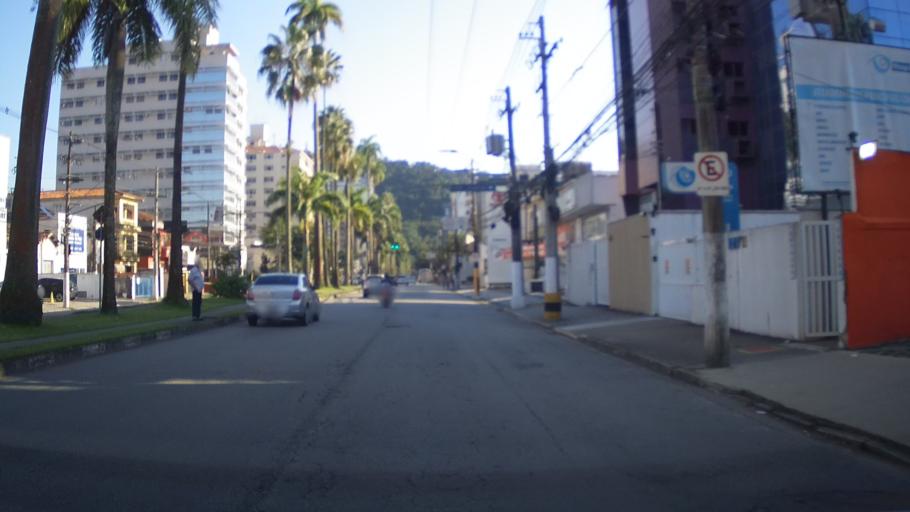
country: BR
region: Sao Paulo
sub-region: Santos
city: Santos
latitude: -23.9493
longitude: -46.3306
